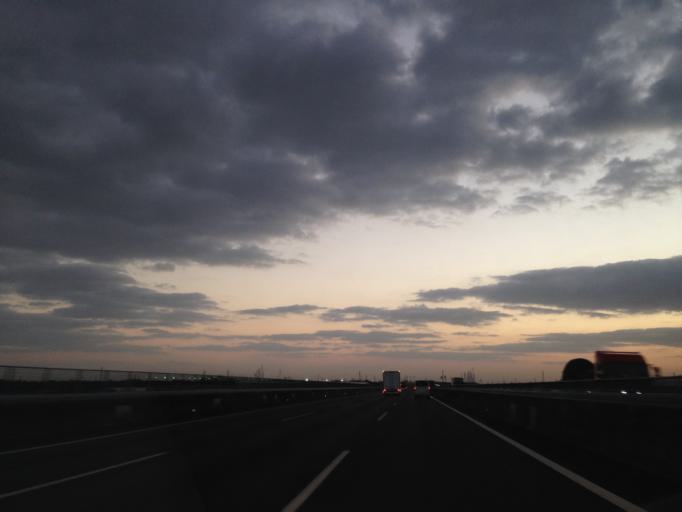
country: JP
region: Aichi
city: Kanie
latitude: 35.0481
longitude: 136.7698
